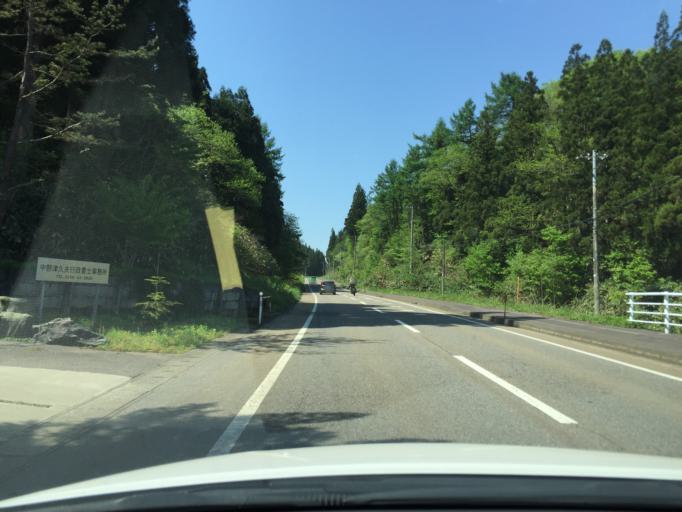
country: JP
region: Niigata
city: Kamo
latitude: 37.6075
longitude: 139.1036
